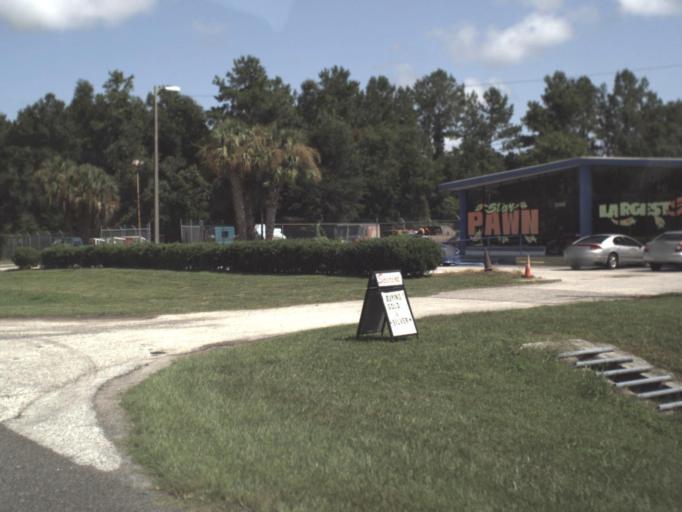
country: US
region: Florida
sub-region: Hernando County
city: Brooksville
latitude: 28.5421
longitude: -82.3653
